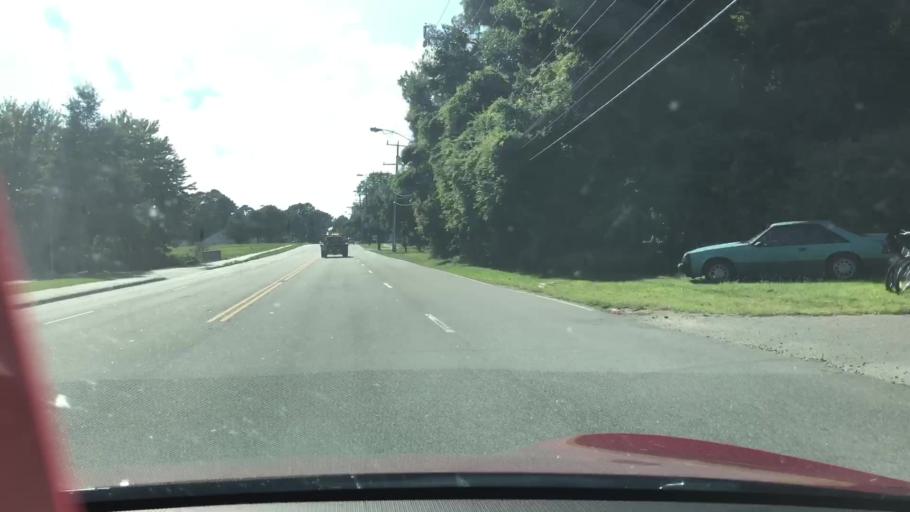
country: US
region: Virginia
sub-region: City of Virginia Beach
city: Virginia Beach
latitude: 36.8427
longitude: -76.0093
